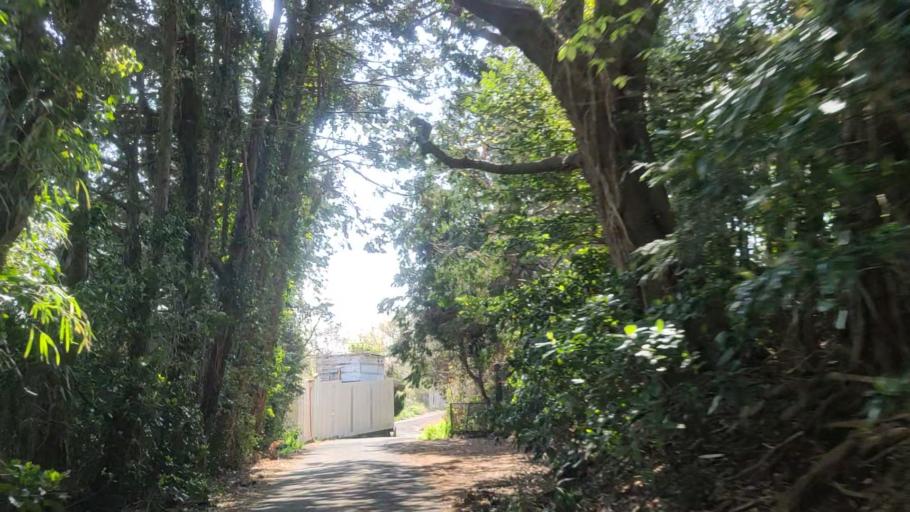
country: JP
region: Kanagawa
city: Ninomiya
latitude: 35.3244
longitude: 139.2706
